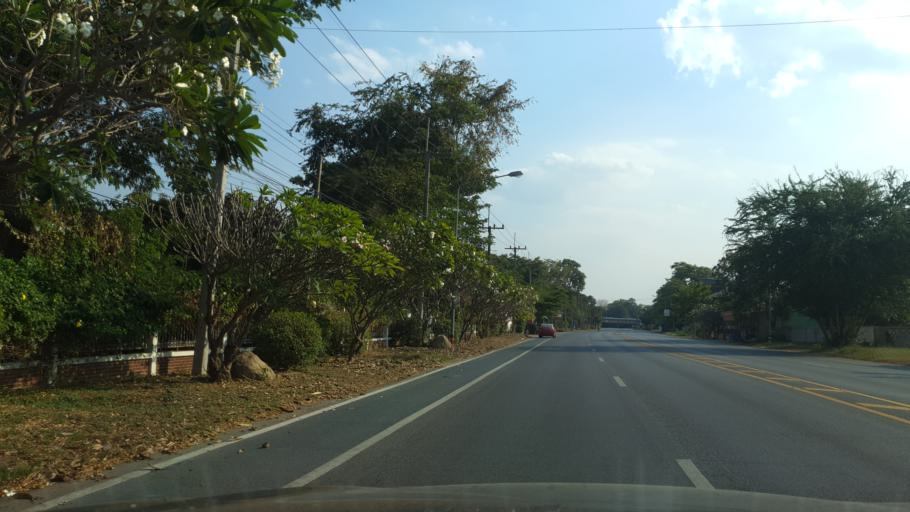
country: TH
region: Tak
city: Tak
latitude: 16.8604
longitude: 99.1214
